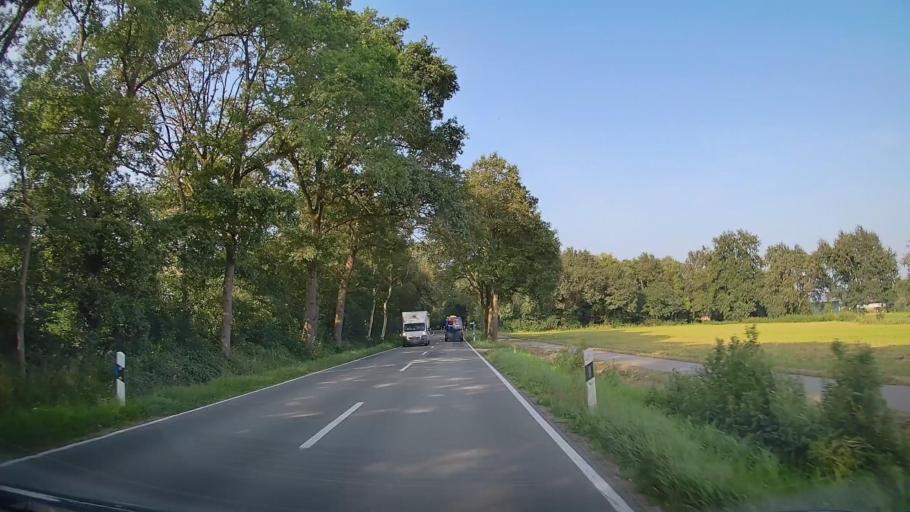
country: DE
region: Lower Saxony
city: Friesoythe
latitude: 53.0890
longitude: 7.8327
